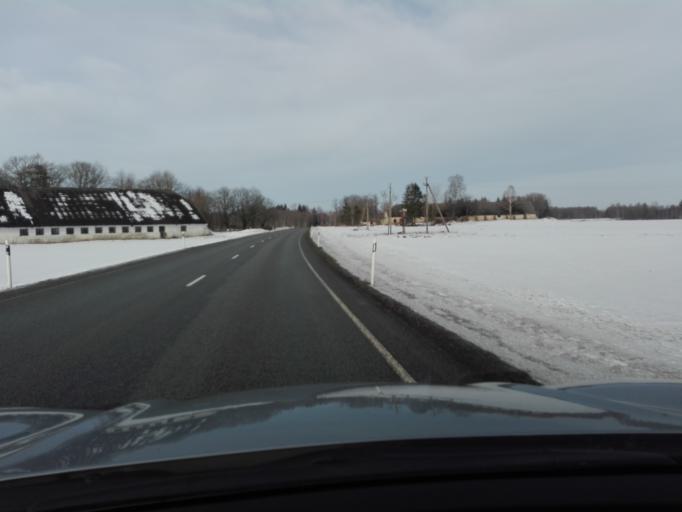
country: EE
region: Raplamaa
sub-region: Rapla vald
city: Rapla
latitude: 58.9185
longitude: 24.7568
